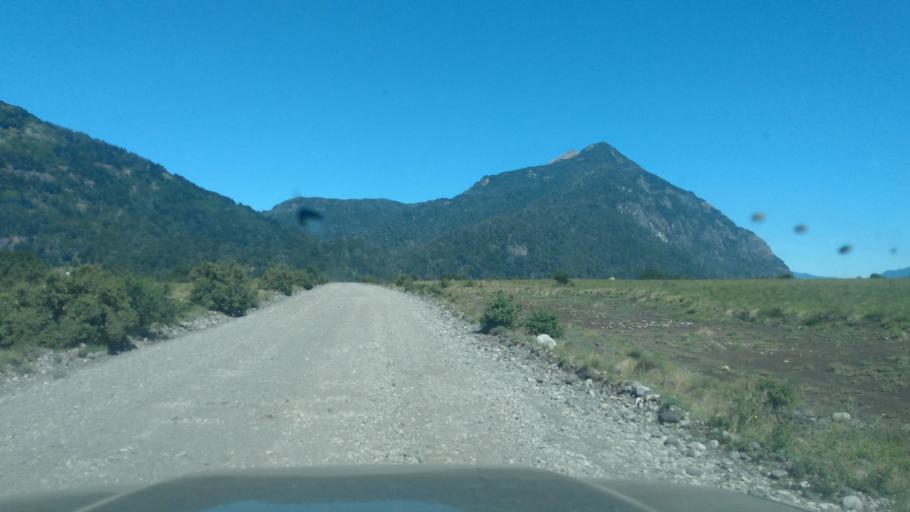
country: AR
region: Neuquen
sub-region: Departamento de Lacar
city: San Martin de los Andes
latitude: -39.7459
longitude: -71.5092
